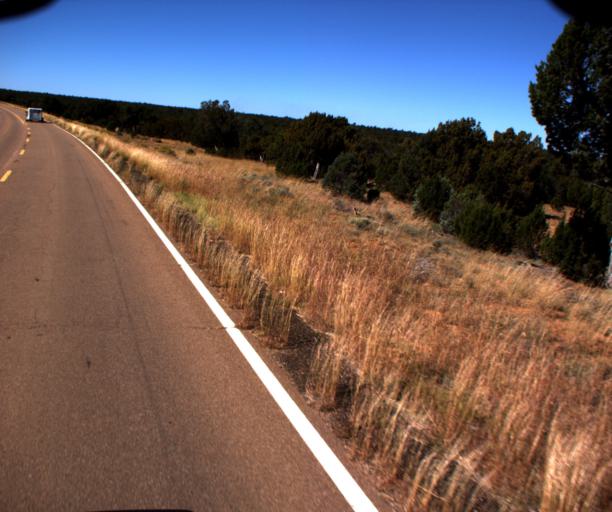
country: US
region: Arizona
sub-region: Navajo County
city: Heber-Overgaard
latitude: 34.4599
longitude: -110.5086
